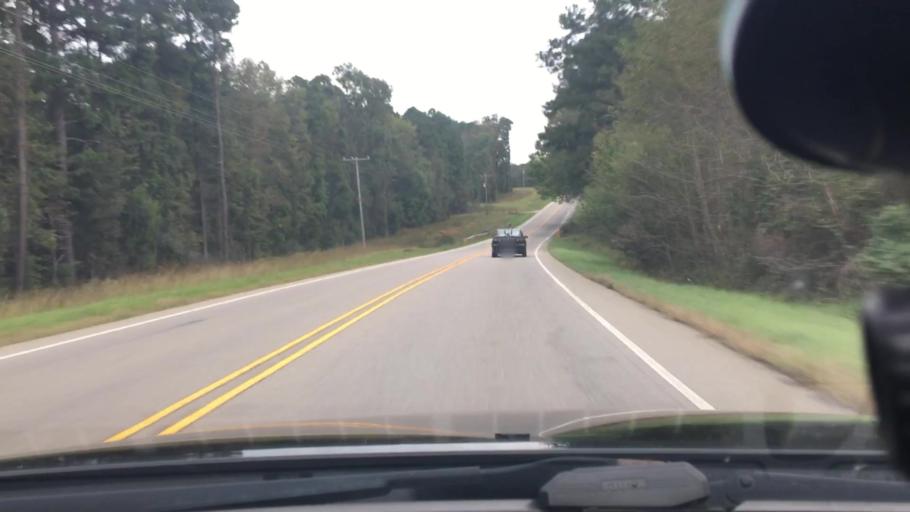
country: US
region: North Carolina
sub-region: Moore County
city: Robbins
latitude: 35.3979
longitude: -79.5376
